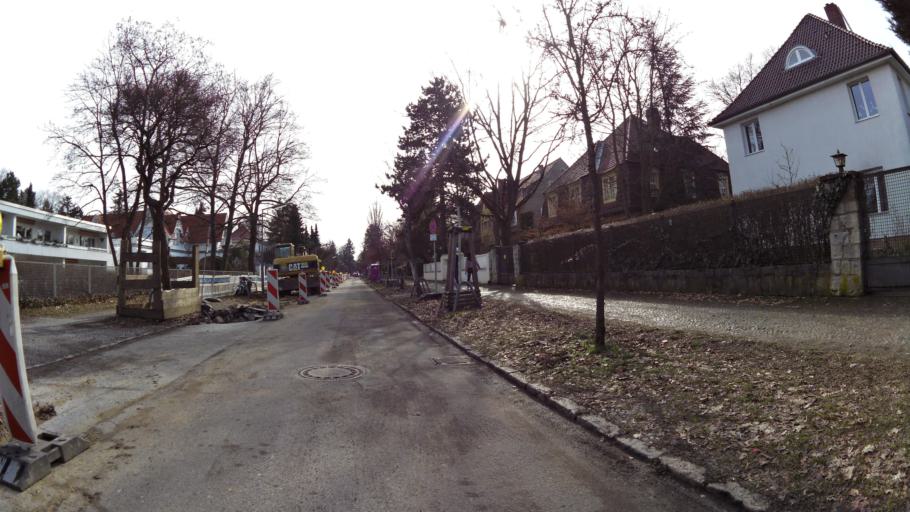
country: DE
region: Berlin
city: Lankwitz
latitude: 52.4399
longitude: 13.3329
